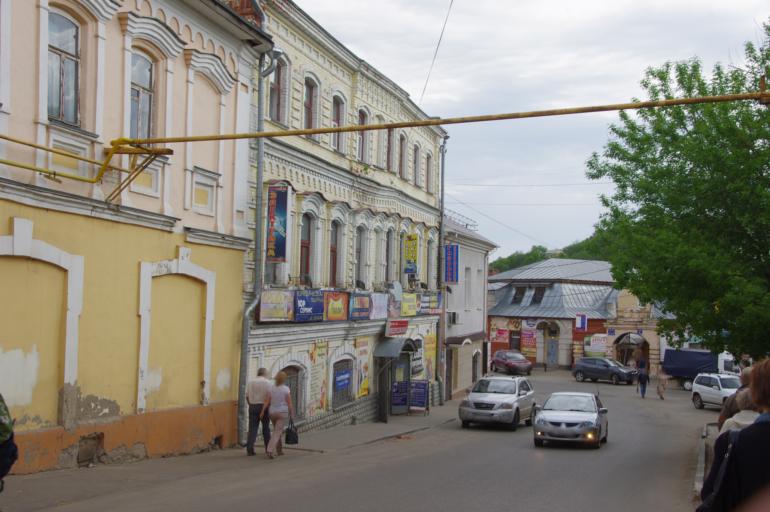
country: RU
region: Nizjnij Novgorod
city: Pavlovo
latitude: 55.9674
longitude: 43.0652
